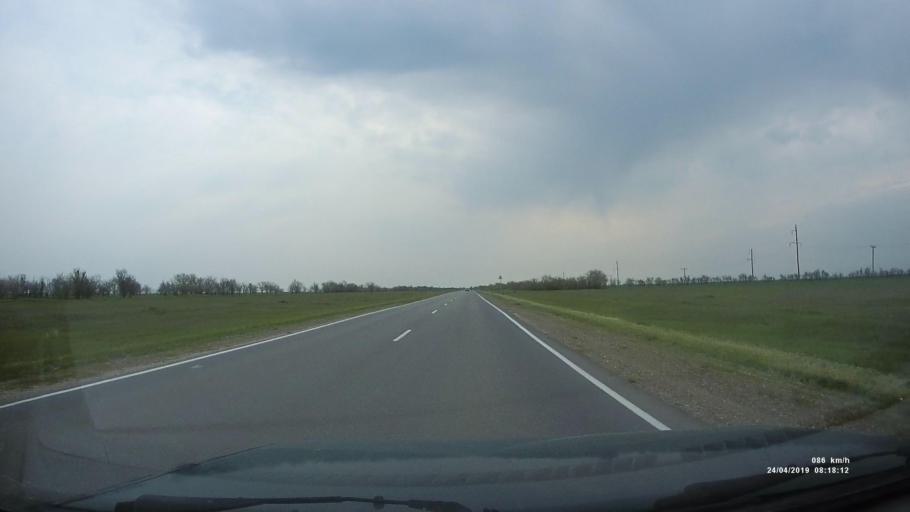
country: RU
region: Kalmykiya
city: Priyutnoye
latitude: 46.1000
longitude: 43.6436
